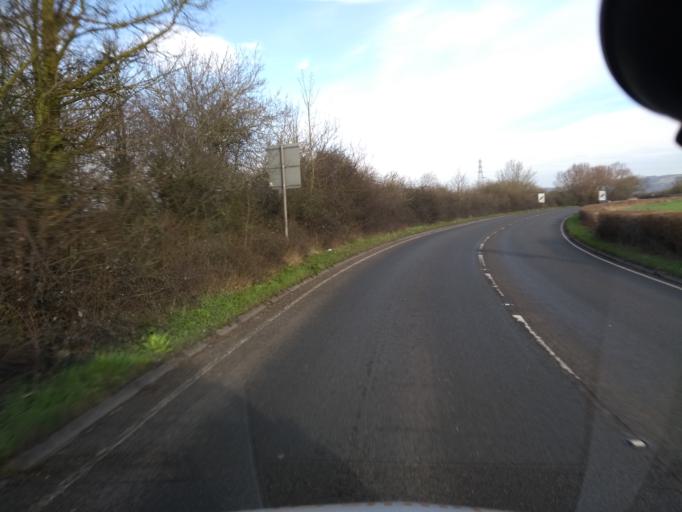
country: GB
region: England
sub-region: North Somerset
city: Bleadon
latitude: 51.2653
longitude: -2.9356
